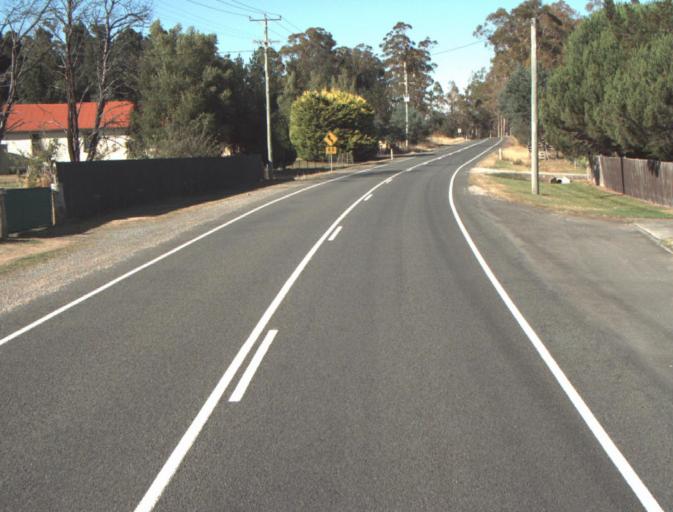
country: AU
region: Tasmania
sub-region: Launceston
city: Newstead
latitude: -41.3940
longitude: 147.2948
